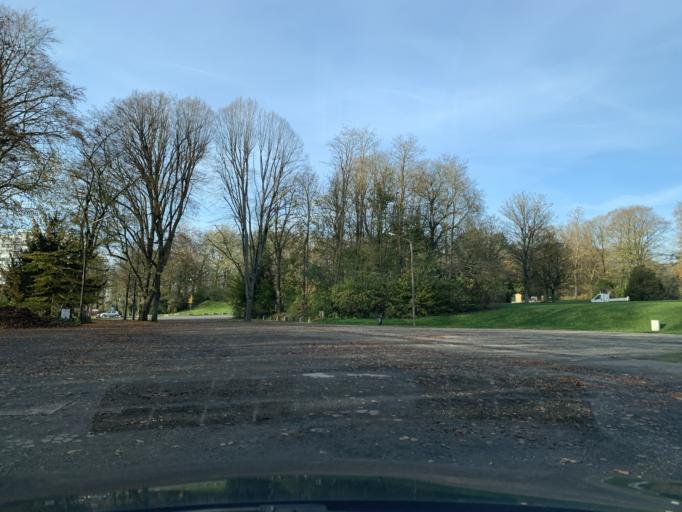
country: FR
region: Nord-Pas-de-Calais
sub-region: Departement du Nord
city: Cambrai
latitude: 50.1699
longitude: 3.2391
